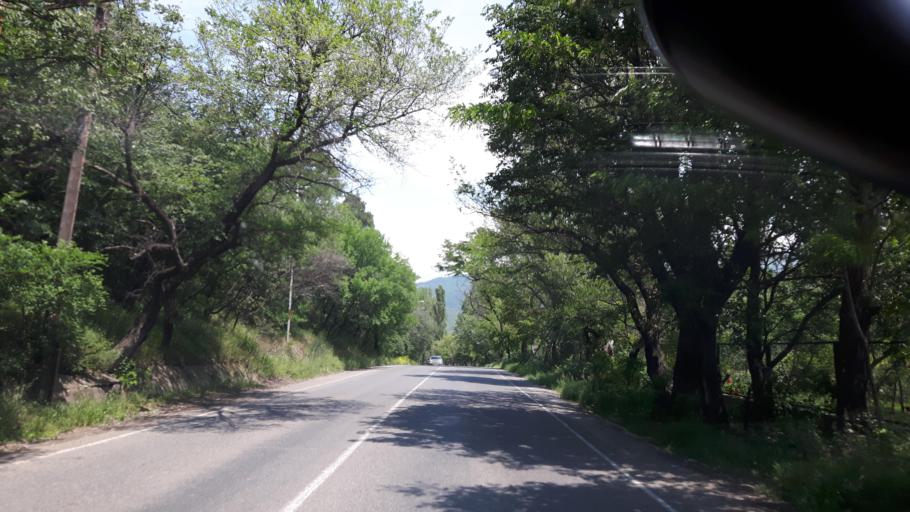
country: GE
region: Mtskheta-Mtianeti
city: Mtskheta
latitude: 41.8349
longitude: 44.7219
